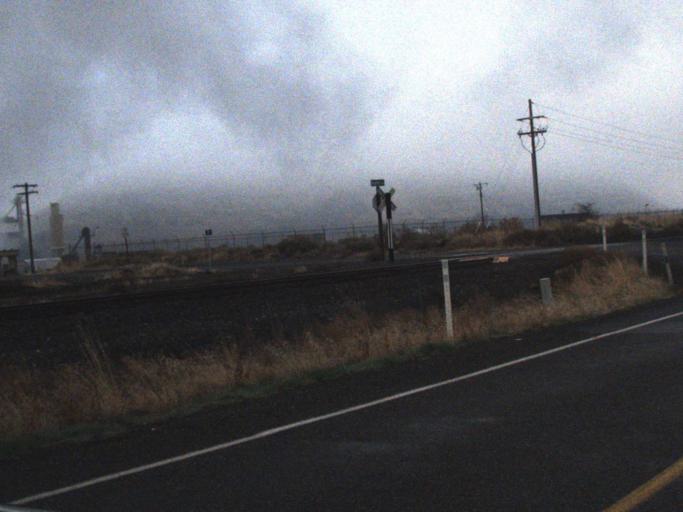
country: US
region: Washington
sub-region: Asotin County
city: Clarkston Heights-Vineland
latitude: 46.4267
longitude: -117.1104
